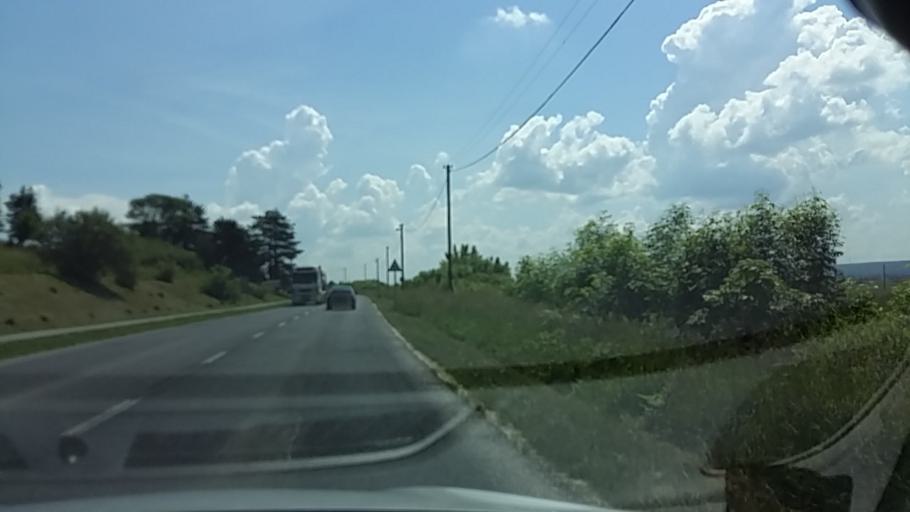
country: AT
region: Burgenland
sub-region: Politischer Bezirk Gussing
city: Inzenhof
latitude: 46.9776
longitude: 16.3535
